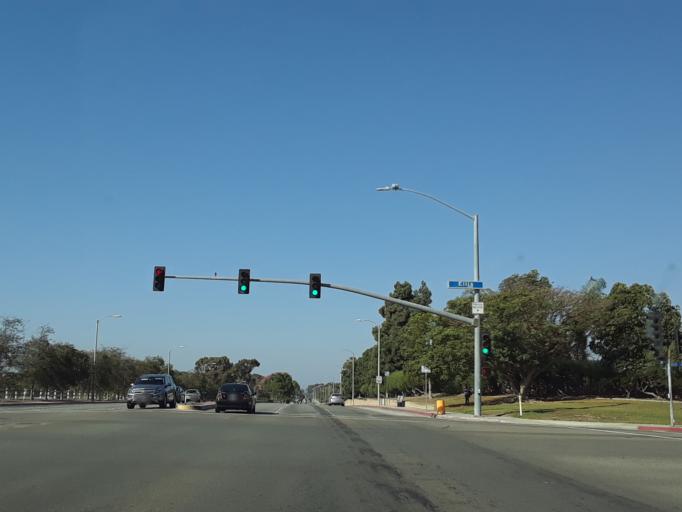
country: US
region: California
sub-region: Orange County
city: Huntington Beach
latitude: 33.6934
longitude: -118.0062
